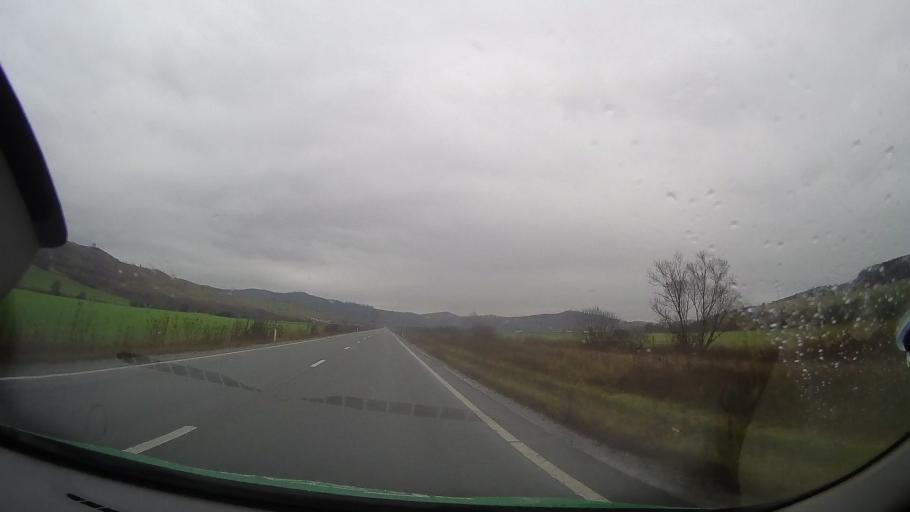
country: RO
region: Bistrita-Nasaud
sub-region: Comuna Teaca
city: Teaca
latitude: 46.9276
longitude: 24.4848
